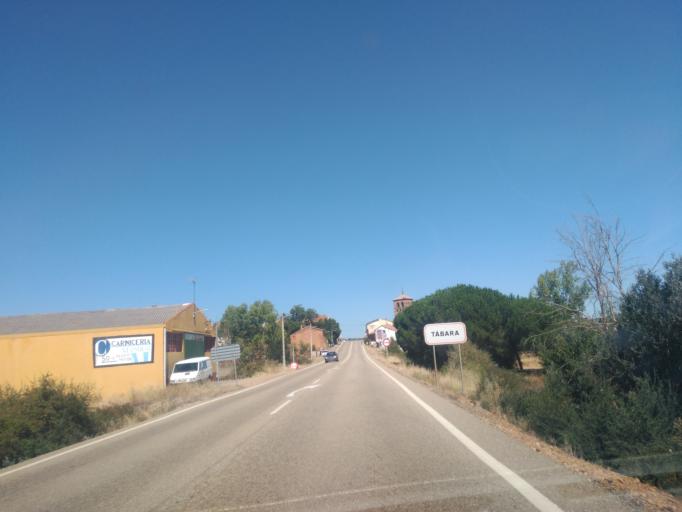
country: ES
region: Castille and Leon
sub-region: Provincia de Zamora
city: Tabara
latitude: 41.8249
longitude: -5.9561
